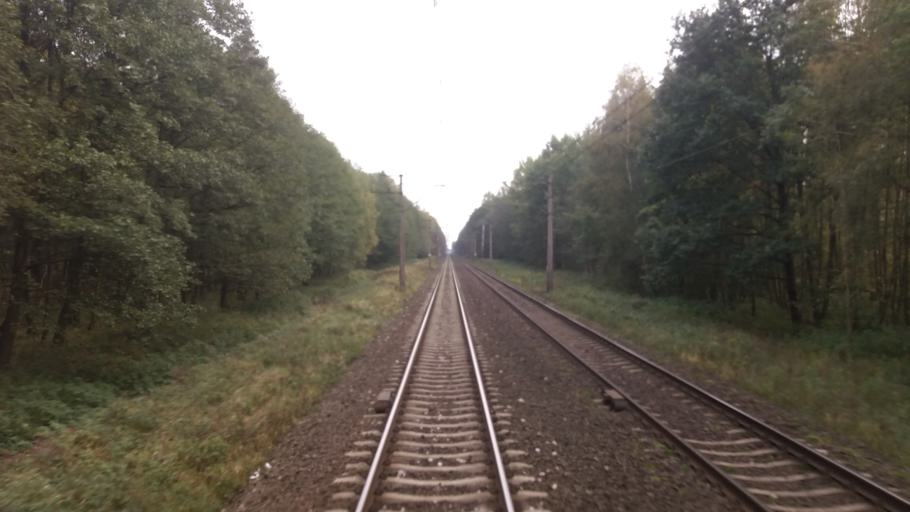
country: PL
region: West Pomeranian Voivodeship
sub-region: Powiat stargardzki
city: Kobylanka
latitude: 53.3766
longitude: 14.8249
